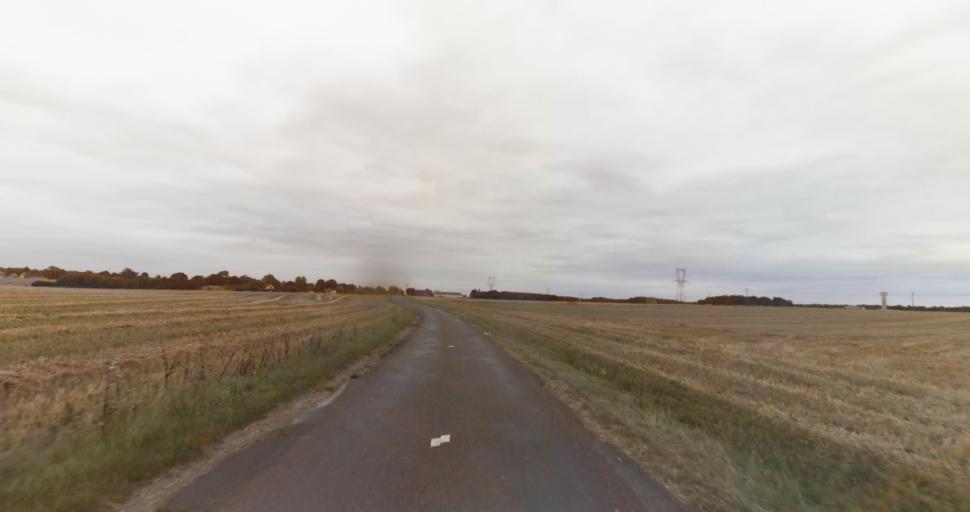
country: FR
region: Haute-Normandie
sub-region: Departement de l'Eure
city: Marcilly-sur-Eure
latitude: 48.8630
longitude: 1.2872
